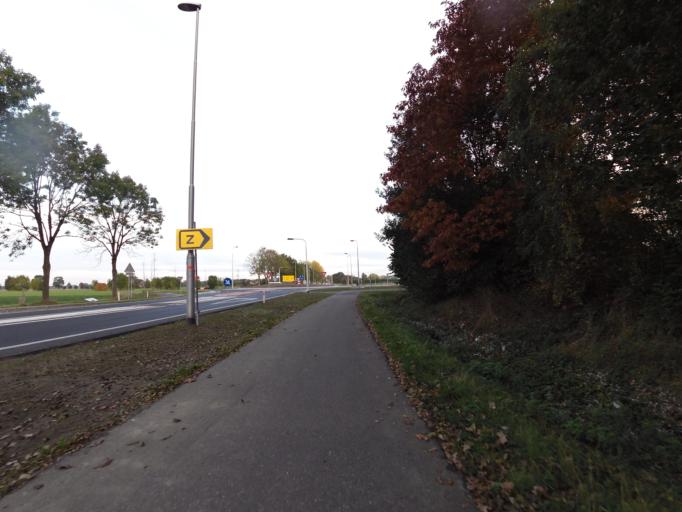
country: NL
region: Gelderland
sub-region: Gemeente Doetinchem
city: Doetinchem
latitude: 51.9651
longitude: 6.2175
